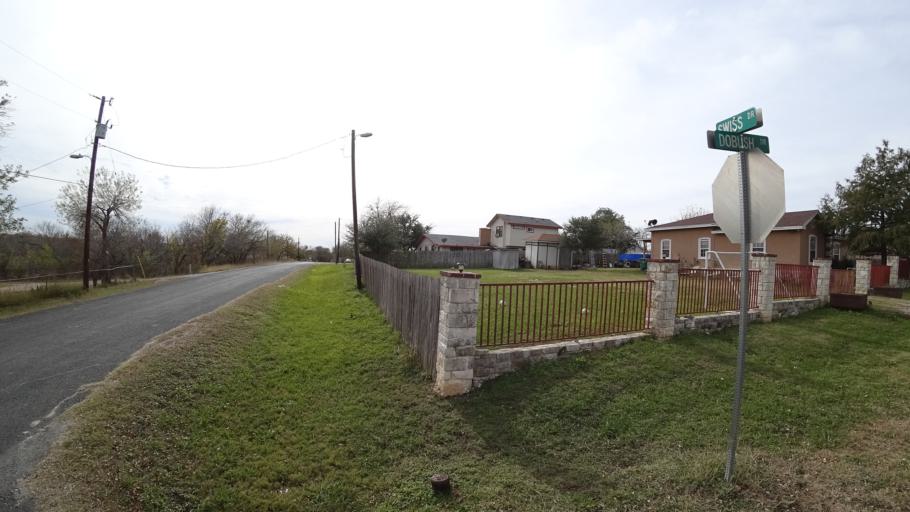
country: US
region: Texas
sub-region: Travis County
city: Garfield
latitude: 30.1280
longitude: -97.6129
